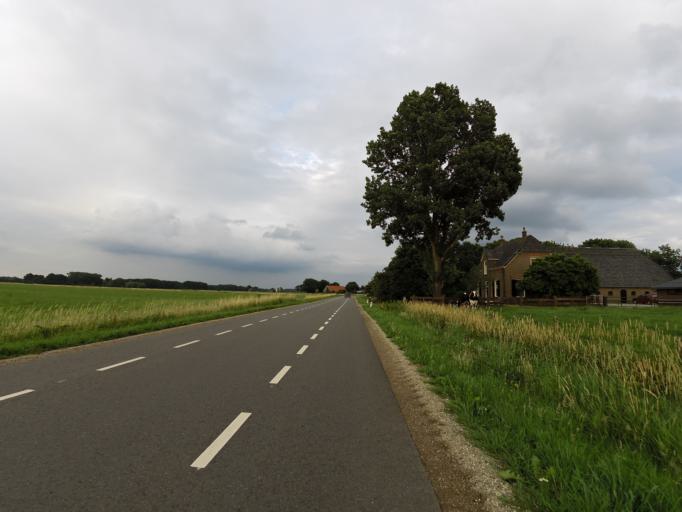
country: NL
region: Gelderland
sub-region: Gemeente Doesburg
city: Doesburg
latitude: 51.9882
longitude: 6.1747
